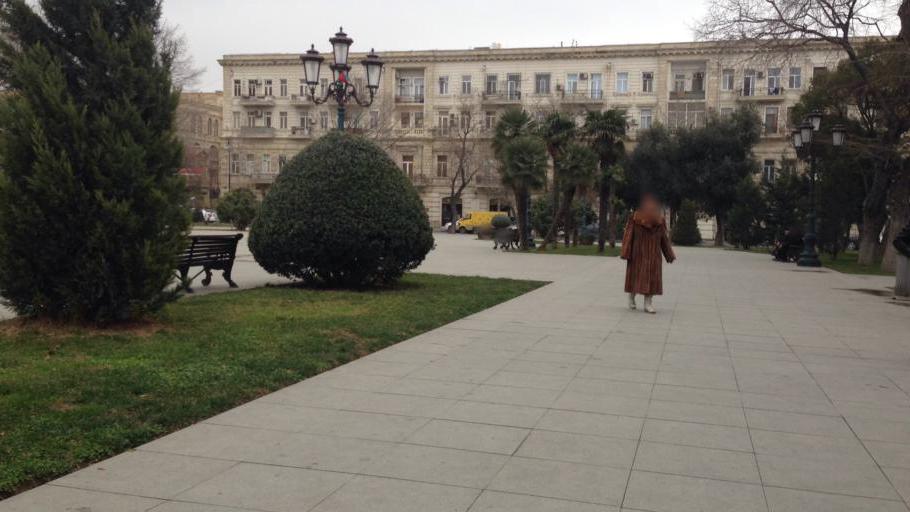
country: AZ
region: Baki
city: Baku
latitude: 40.3732
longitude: 49.8463
